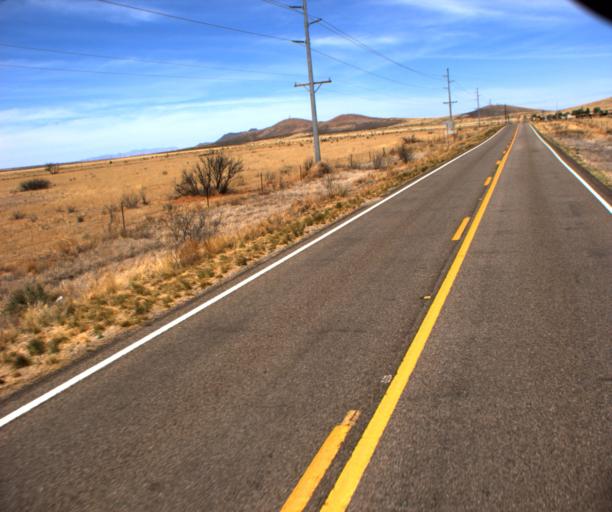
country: US
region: Arizona
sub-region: Cochise County
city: Willcox
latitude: 31.8775
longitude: -109.6951
